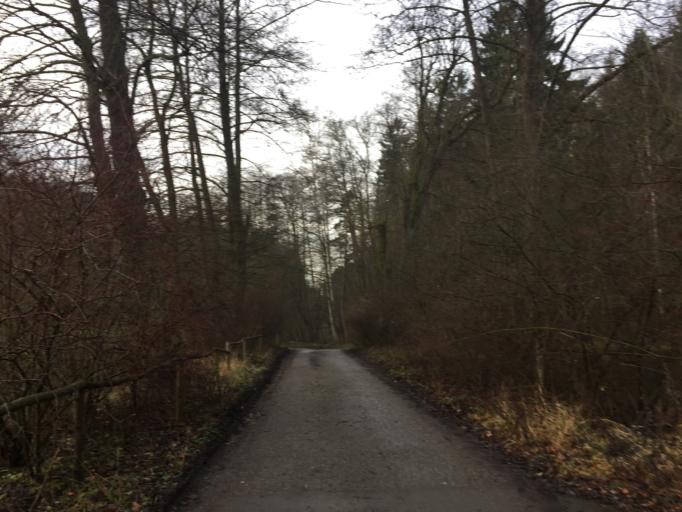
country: DE
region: Thuringia
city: Schleifreisen
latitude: 50.8938
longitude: 11.8215
